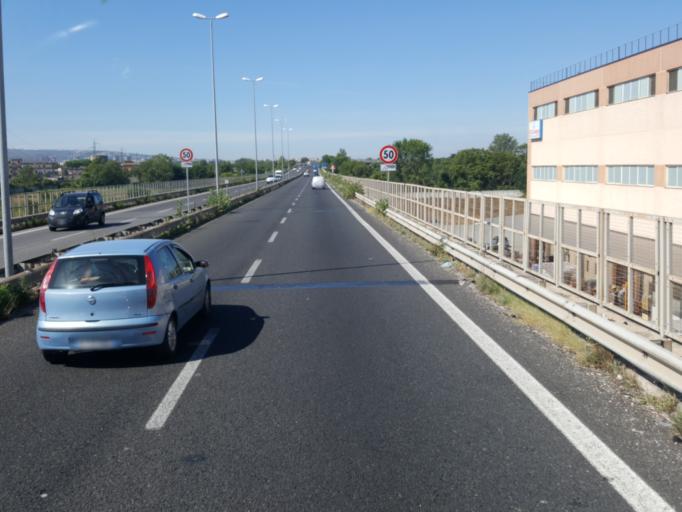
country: IT
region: Campania
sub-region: Provincia di Napoli
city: Frattamaggiore
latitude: 40.9282
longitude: 14.2720
